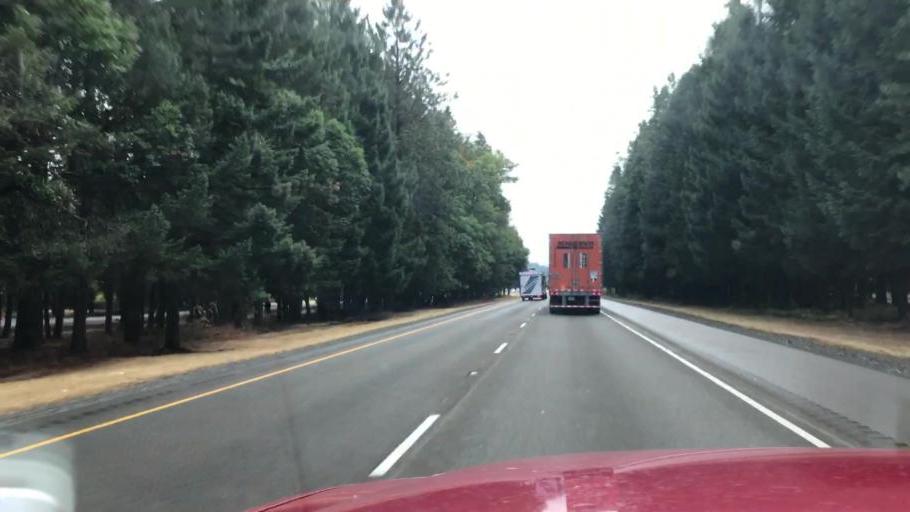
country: US
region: Oregon
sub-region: Douglas County
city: Canyonville
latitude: 42.7563
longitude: -123.3532
